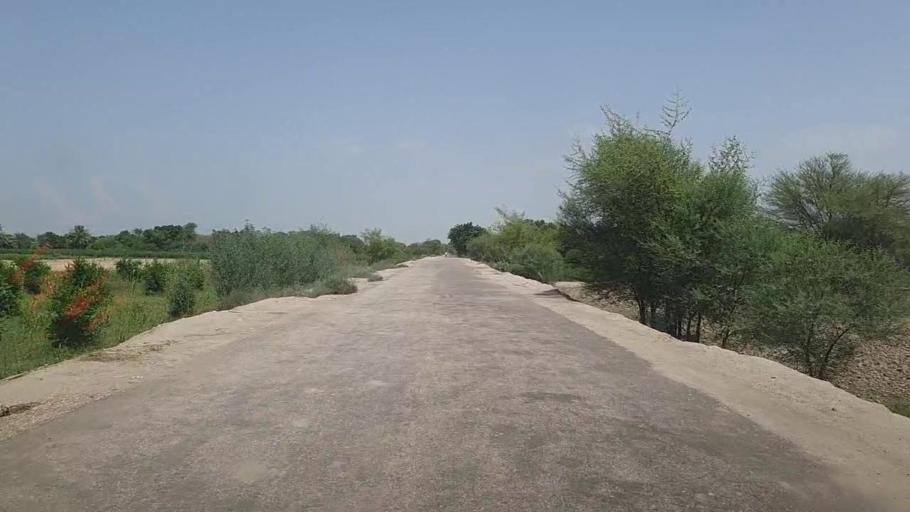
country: PK
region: Sindh
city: Pad Idan
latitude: 26.8430
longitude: 68.3392
